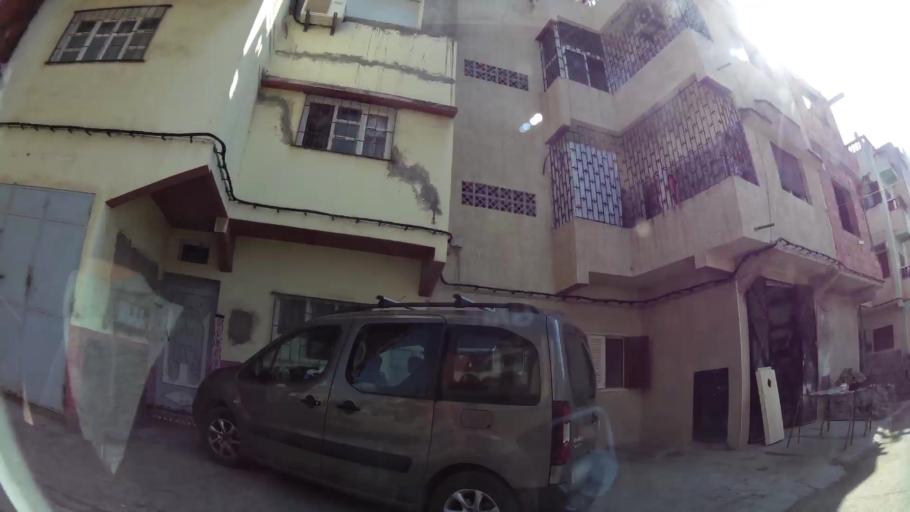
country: MA
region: Rabat-Sale-Zemmour-Zaer
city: Sale
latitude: 34.0435
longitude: -6.7783
